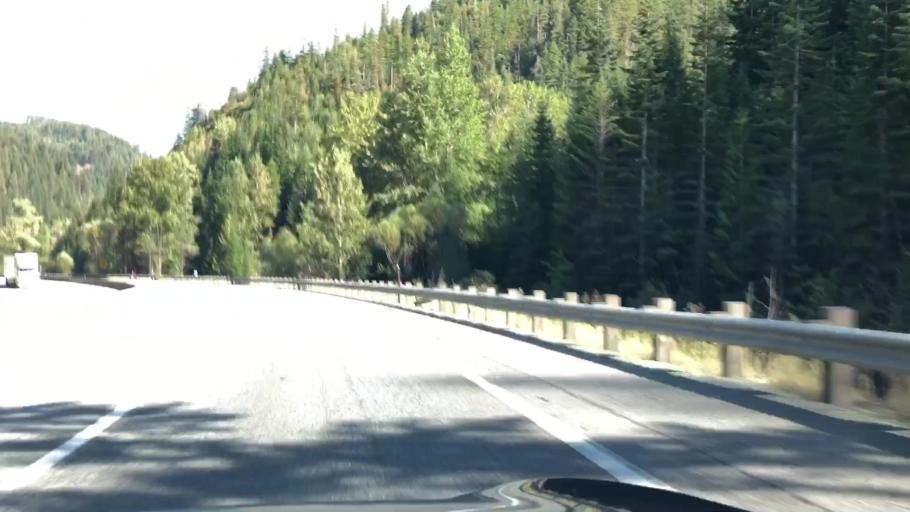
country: US
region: Idaho
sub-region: Shoshone County
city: Wallace
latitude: 47.4687
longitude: -115.8590
